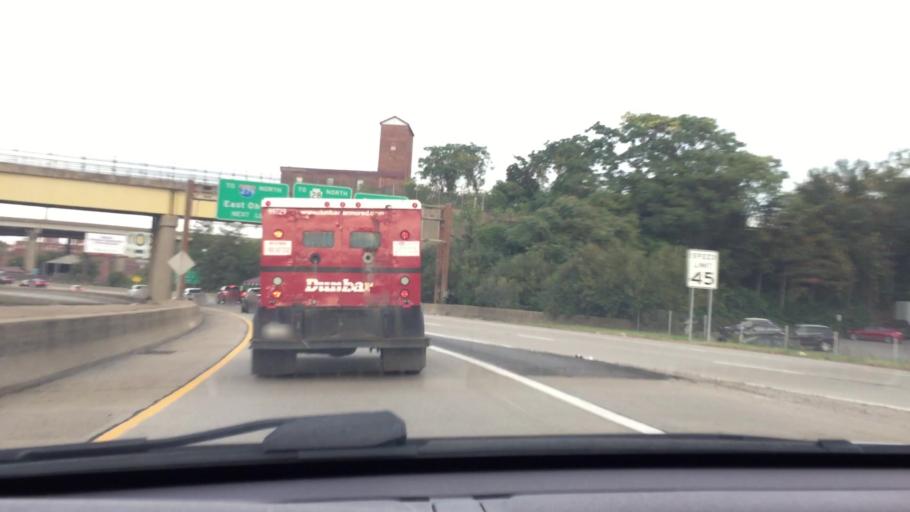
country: US
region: Pennsylvania
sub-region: Allegheny County
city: Pittsburgh
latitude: 40.4497
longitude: -79.9985
